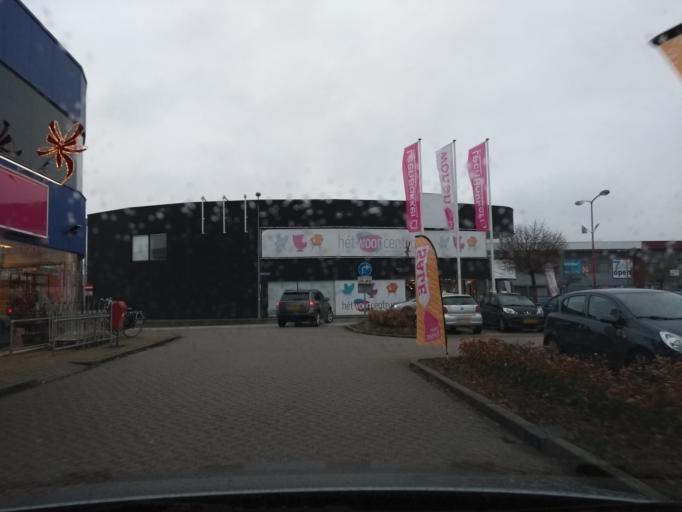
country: NL
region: Overijssel
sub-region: Gemeente Almelo
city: Almelo
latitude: 52.3407
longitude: 6.6411
